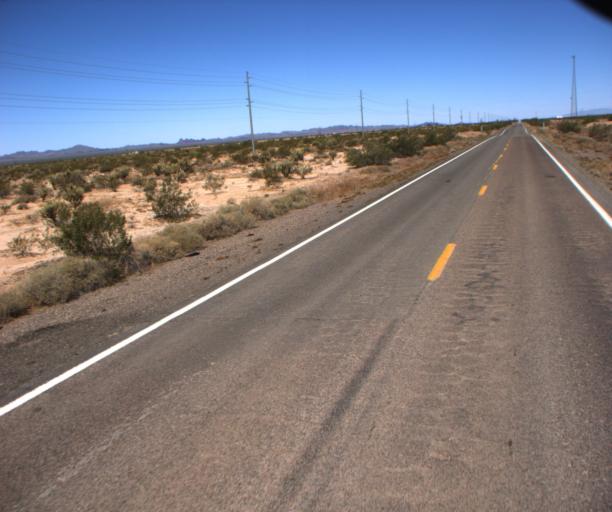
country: US
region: Arizona
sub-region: La Paz County
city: Salome
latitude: 33.8332
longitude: -113.8796
